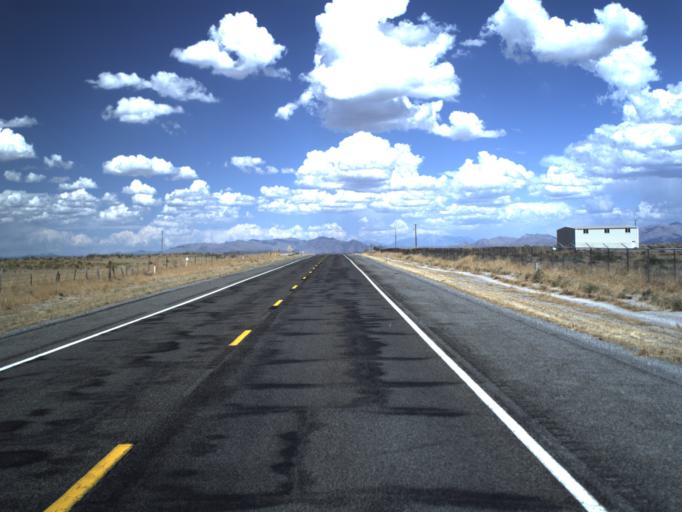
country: US
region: Utah
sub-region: Millard County
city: Delta
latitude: 39.3862
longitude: -112.5179
